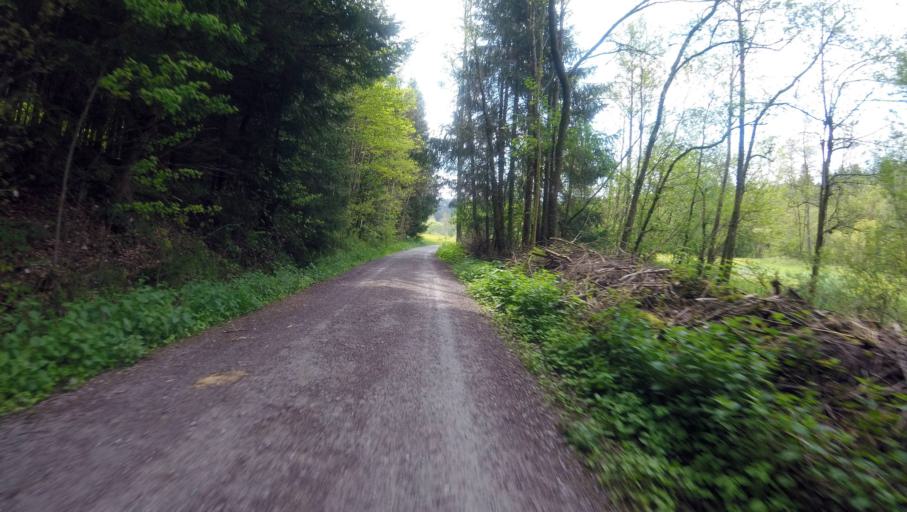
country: DE
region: Baden-Wuerttemberg
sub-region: Regierungsbezirk Stuttgart
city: Spraitbach
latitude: 48.8601
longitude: 9.7579
